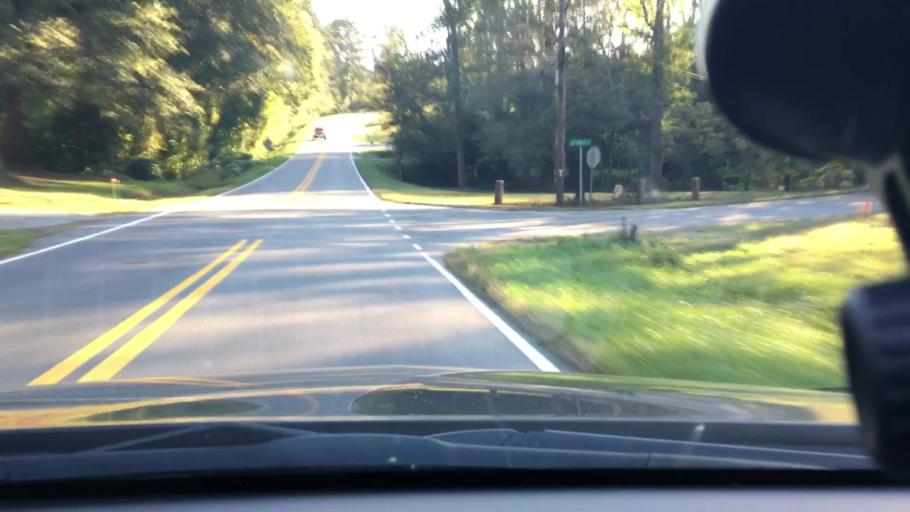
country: US
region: North Carolina
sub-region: Rutherford County
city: Rutherfordton
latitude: 35.3628
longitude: -81.9716
